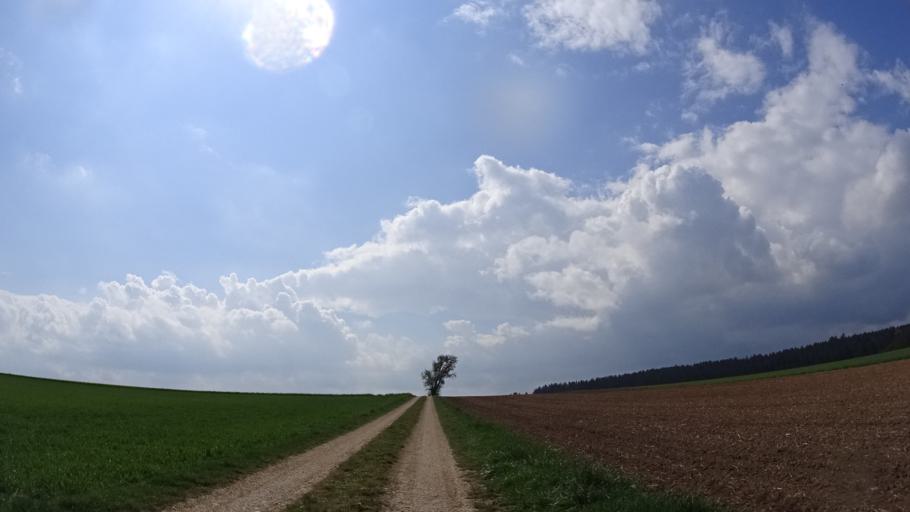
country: DE
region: Bavaria
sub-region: Upper Bavaria
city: Hitzhofen
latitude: 48.8690
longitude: 11.3107
